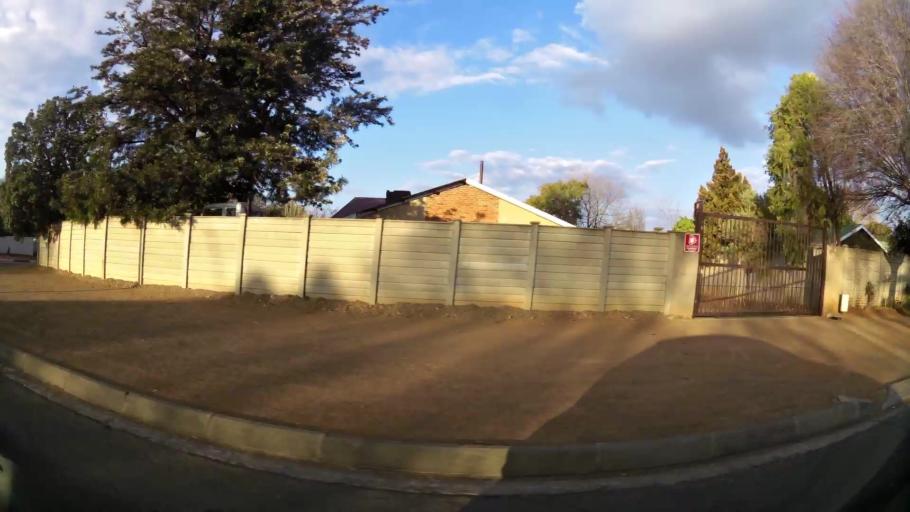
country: ZA
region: Orange Free State
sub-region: Mangaung Metropolitan Municipality
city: Bloemfontein
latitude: -29.1396
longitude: 26.1840
